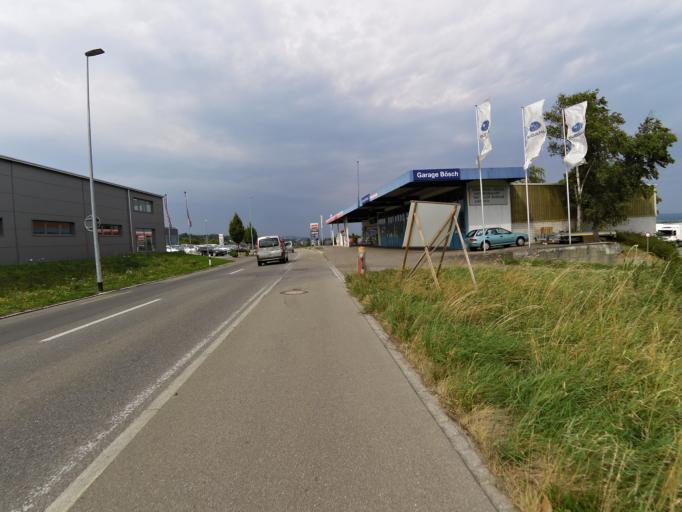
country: CH
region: Thurgau
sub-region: Kreuzlingen District
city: Tagerwilen
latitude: 47.6594
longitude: 9.1231
